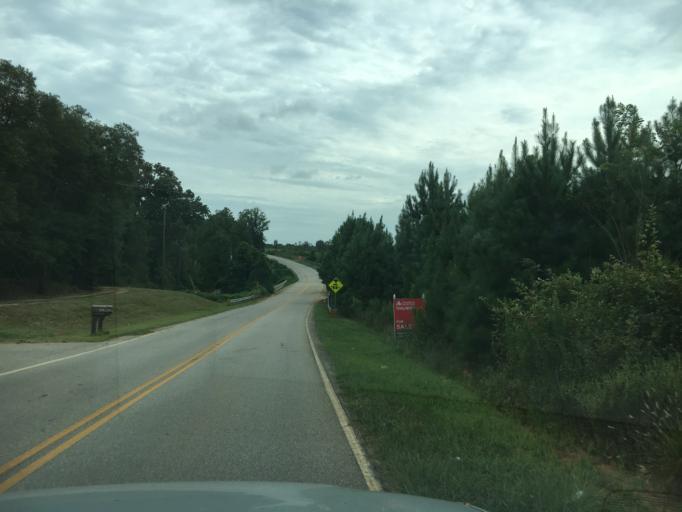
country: US
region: South Carolina
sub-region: Spartanburg County
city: Duncan
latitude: 34.9335
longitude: -82.1675
